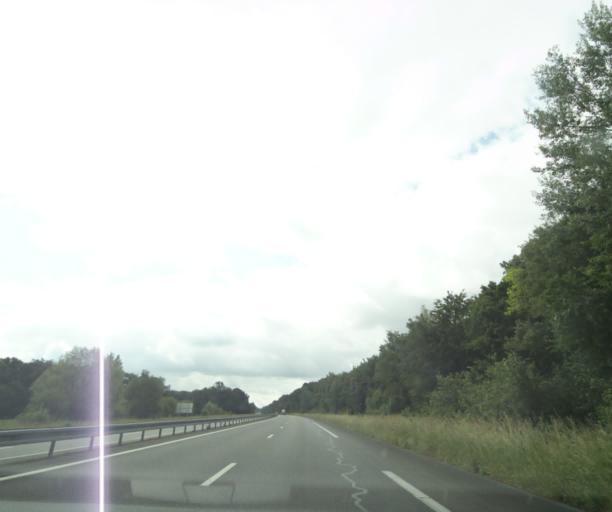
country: FR
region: Pays de la Loire
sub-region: Departement de Maine-et-Loire
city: Baune
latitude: 47.5206
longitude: -0.3072
